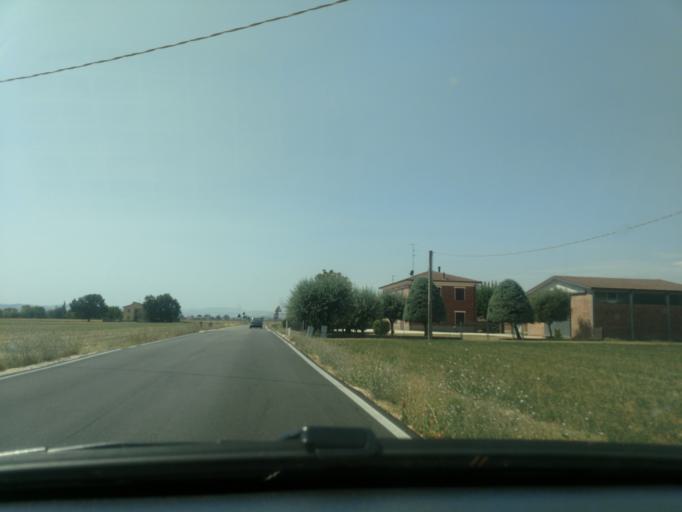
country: IT
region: Emilia-Romagna
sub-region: Provincia di Bologna
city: Medicina-Buda
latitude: 44.4388
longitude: 11.6301
